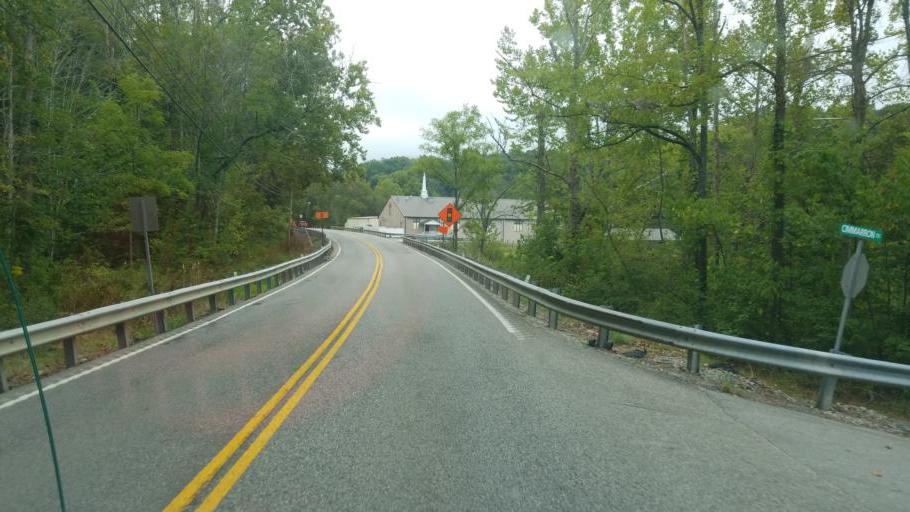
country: US
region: Kentucky
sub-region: Rowan County
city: Morehead
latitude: 38.2092
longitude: -83.4694
